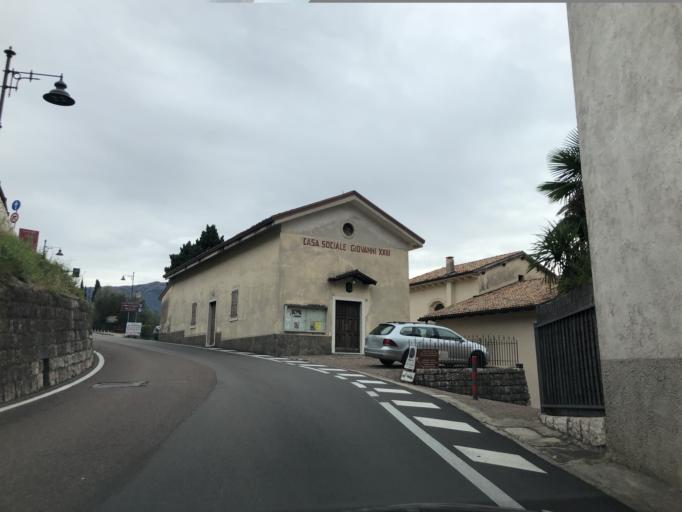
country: IT
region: Trentino-Alto Adige
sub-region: Provincia di Trento
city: Tenno
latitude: 45.9147
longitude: 10.8429
